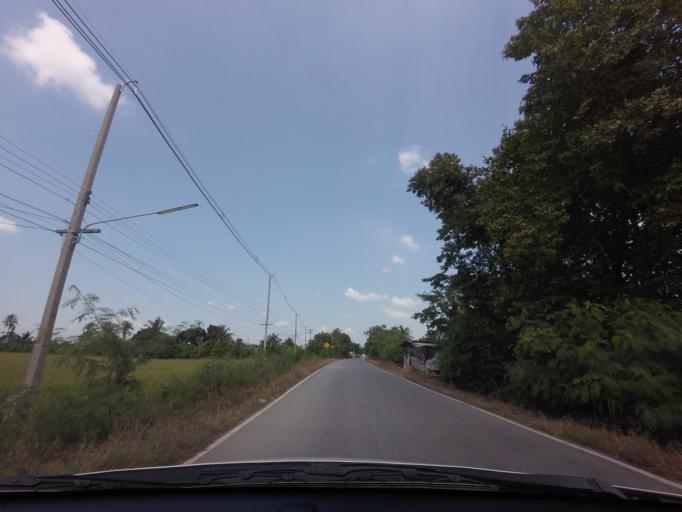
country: TH
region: Nakhon Pathom
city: Nakhon Chai Si
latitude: 13.8055
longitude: 100.1974
